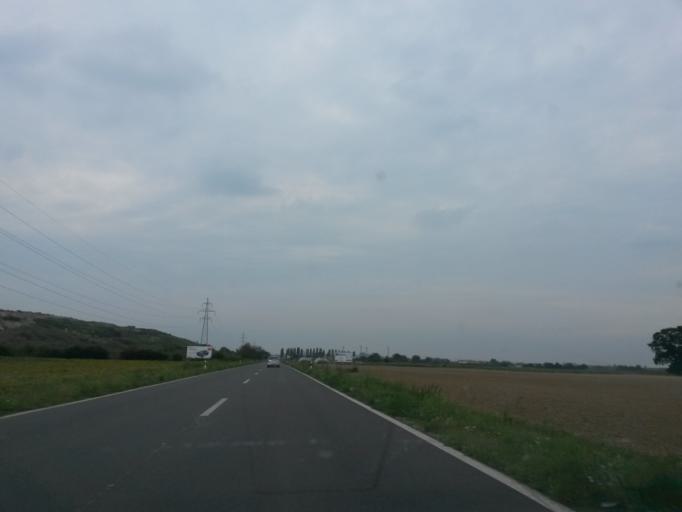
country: HR
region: Osjecko-Baranjska
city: Brijest
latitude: 45.5275
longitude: 18.6873
